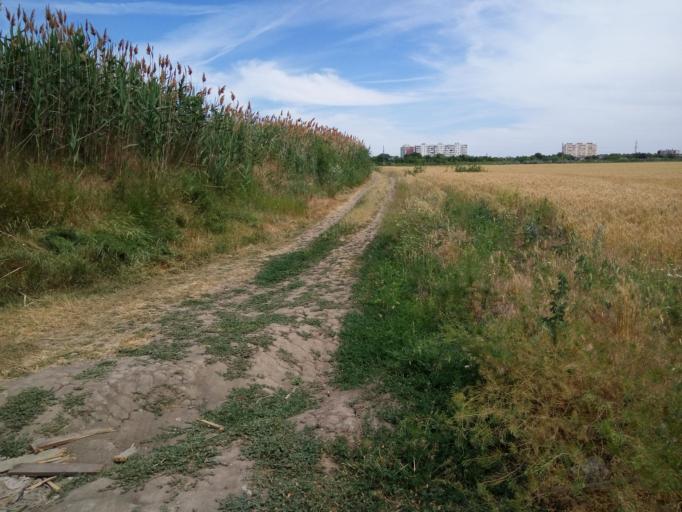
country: RU
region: Rostov
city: Bataysk
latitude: 47.1213
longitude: 39.7229
